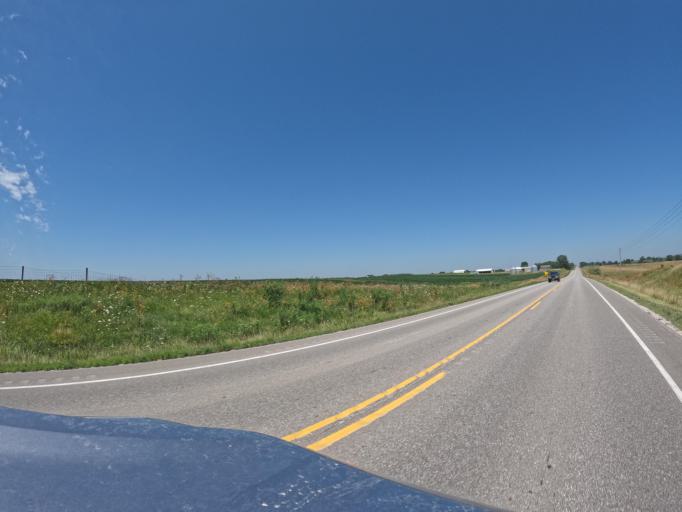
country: US
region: Iowa
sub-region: Keokuk County
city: Sigourney
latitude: 41.4552
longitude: -92.3551
